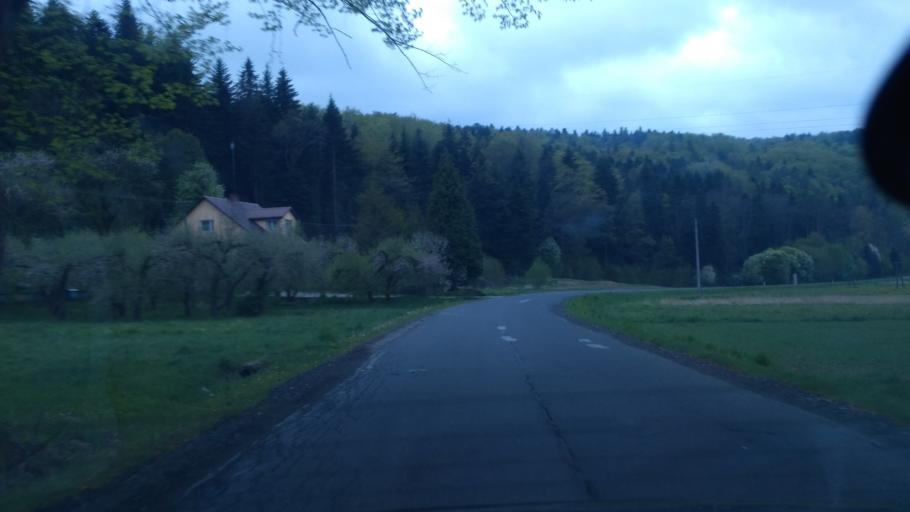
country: PL
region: Subcarpathian Voivodeship
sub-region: Powiat brzozowski
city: Nozdrzec
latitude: 49.7310
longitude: 22.2094
